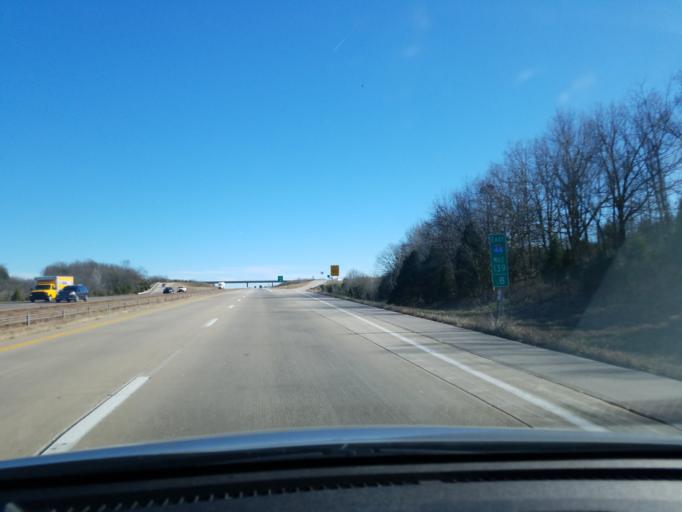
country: US
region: Missouri
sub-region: Pulaski County
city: Richland
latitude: 37.7578
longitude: -92.5109
